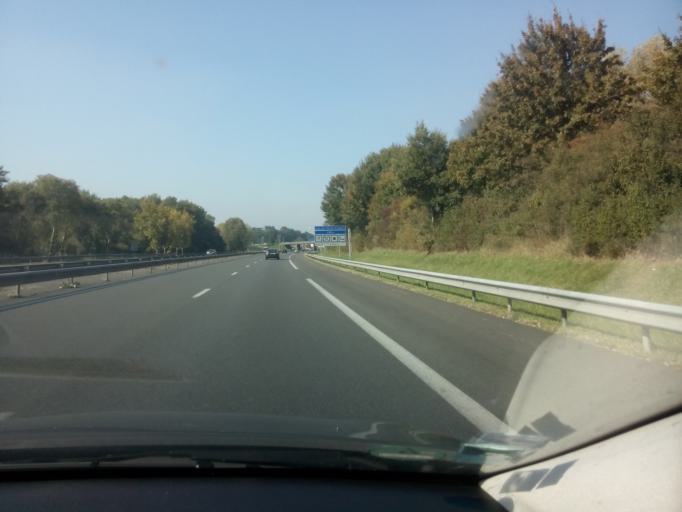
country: FR
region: Pays de la Loire
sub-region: Departement de Maine-et-Loire
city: Pellouailles-les-Vignes
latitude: 47.5004
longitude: -0.4813
